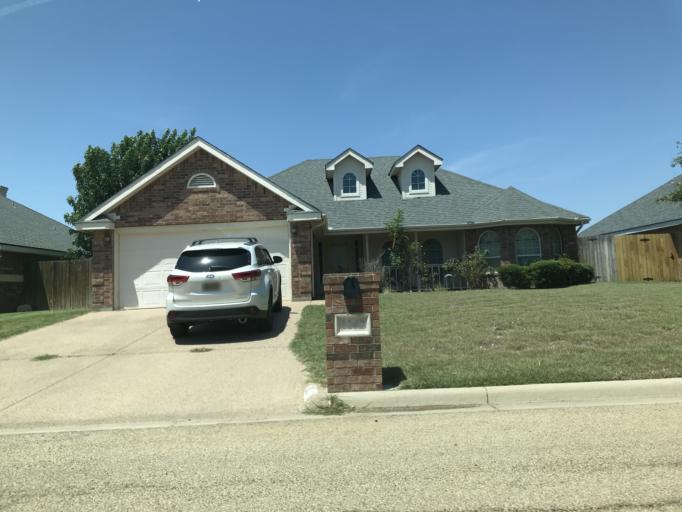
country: US
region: Texas
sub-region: Taylor County
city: Abilene
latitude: 32.4902
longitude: -99.6871
